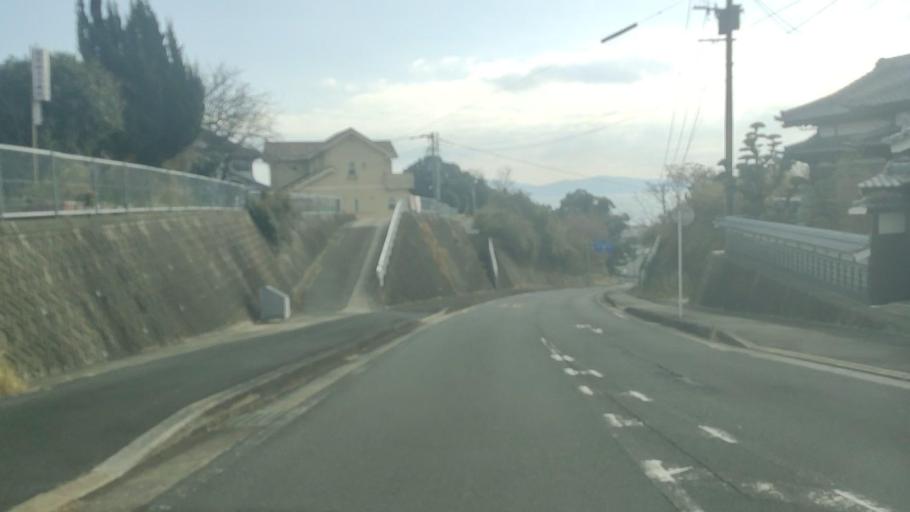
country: JP
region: Nagasaki
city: Shimabara
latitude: 32.6591
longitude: 130.2886
